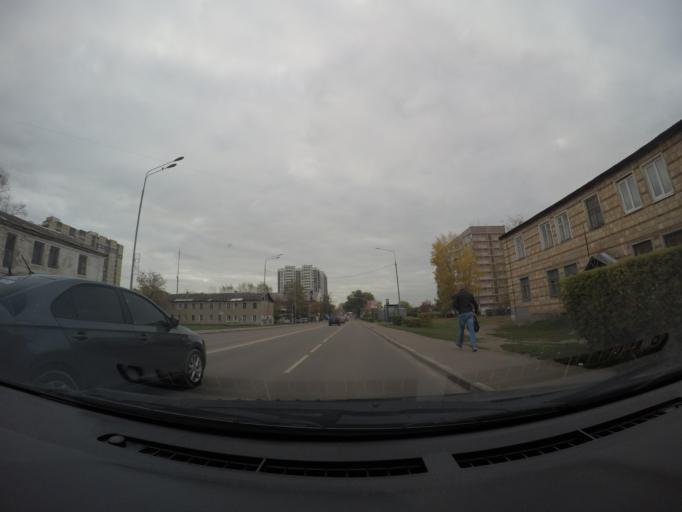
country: RU
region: Moskovskaya
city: Staraya Kupavna
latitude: 55.8045
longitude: 38.1803
